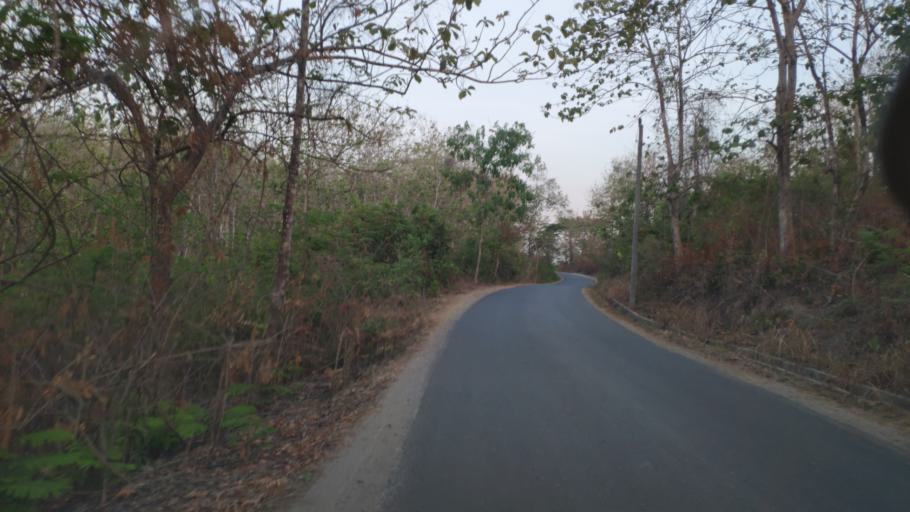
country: ID
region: Central Java
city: Semanggi
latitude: -7.0769
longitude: 111.4185
